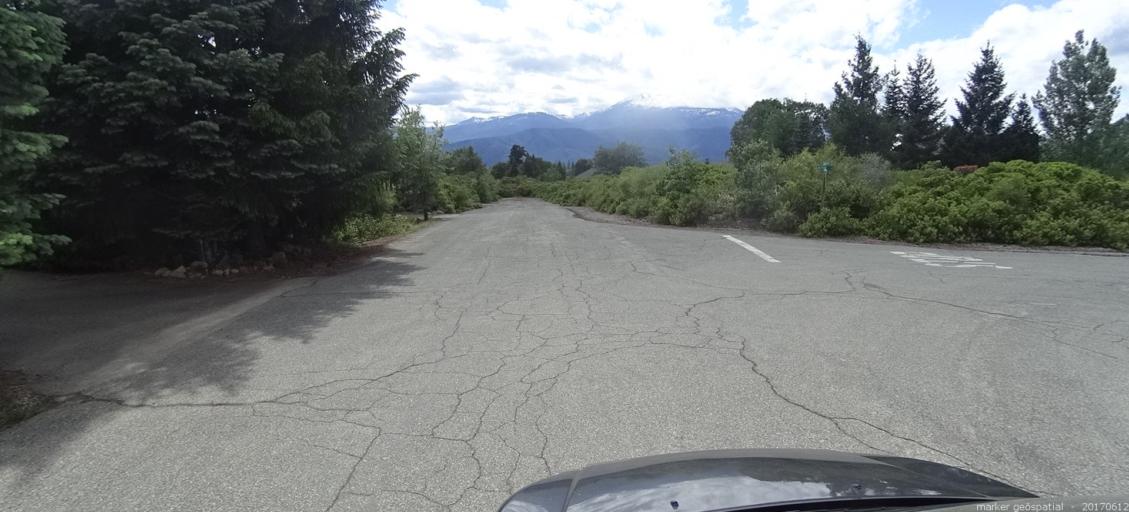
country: US
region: California
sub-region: Siskiyou County
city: Mount Shasta
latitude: 41.3153
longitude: -122.2867
